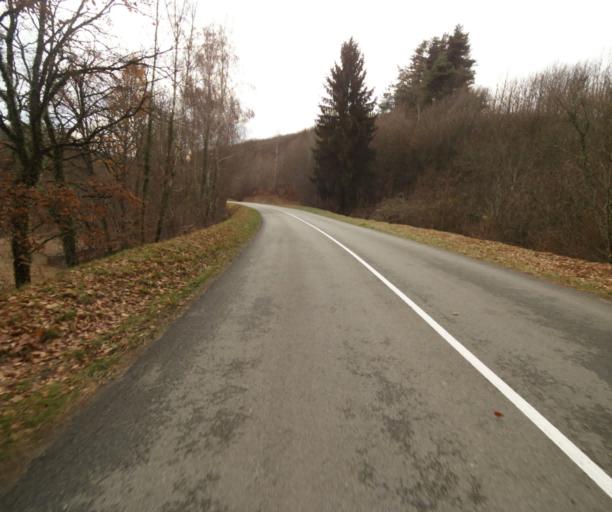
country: FR
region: Limousin
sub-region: Departement de la Correze
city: Chameyrat
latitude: 45.2634
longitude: 1.7057
